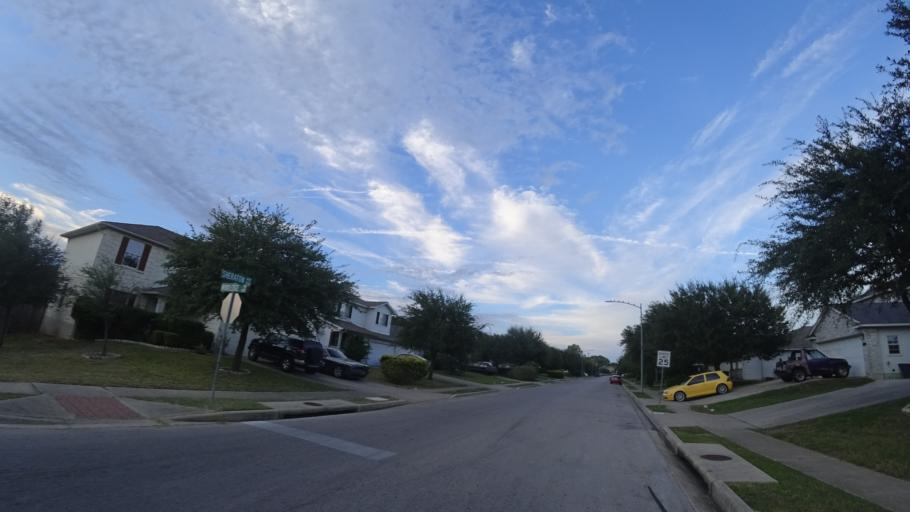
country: US
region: Texas
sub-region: Travis County
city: Austin
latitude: 30.2096
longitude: -97.7629
